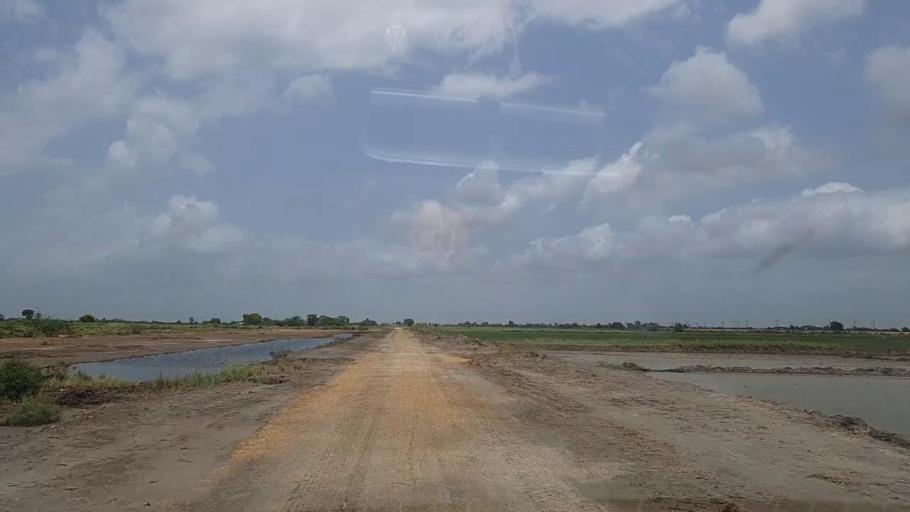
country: PK
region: Sindh
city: Thatta
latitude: 24.6215
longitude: 68.0376
